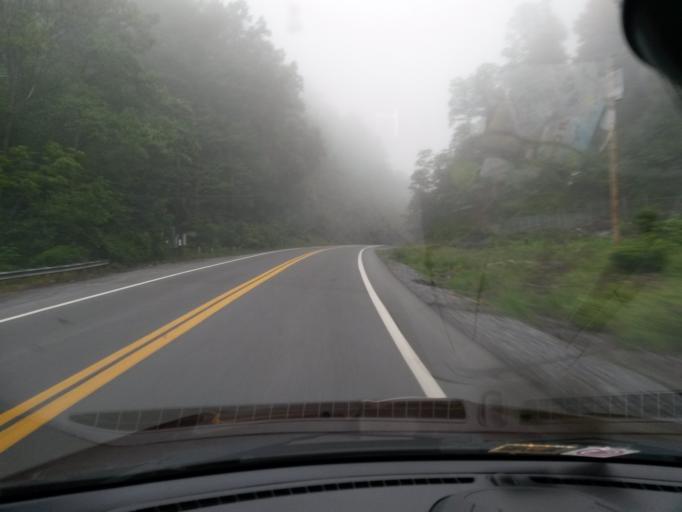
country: US
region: West Virginia
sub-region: Wyoming County
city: Pineville
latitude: 37.5520
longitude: -81.5503
